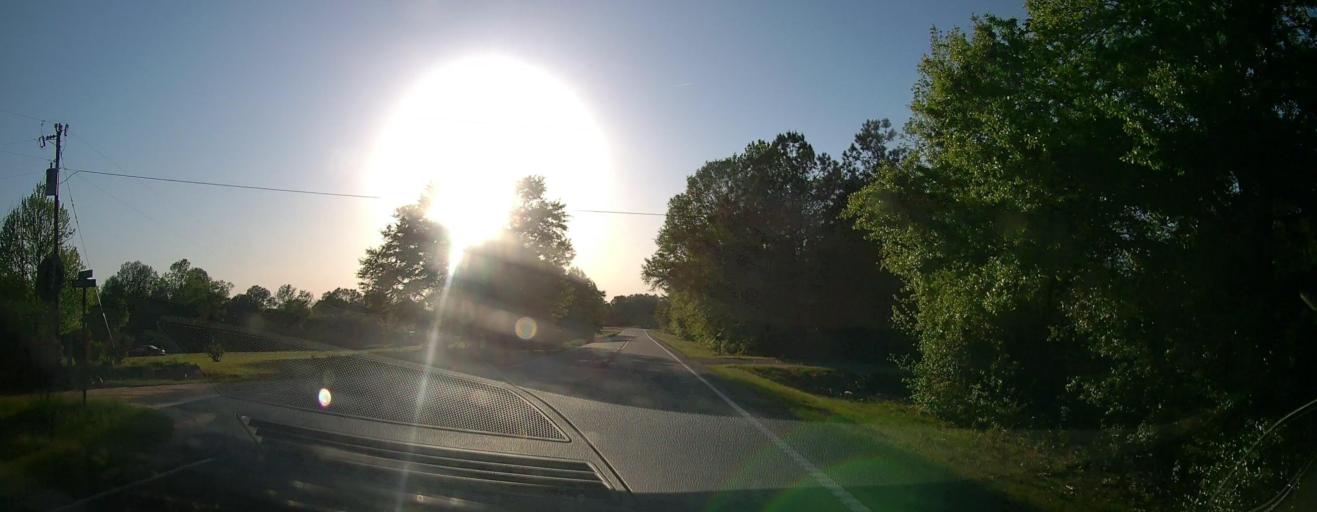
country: US
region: Georgia
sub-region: Schley County
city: Ellaville
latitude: 32.3448
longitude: -84.3672
